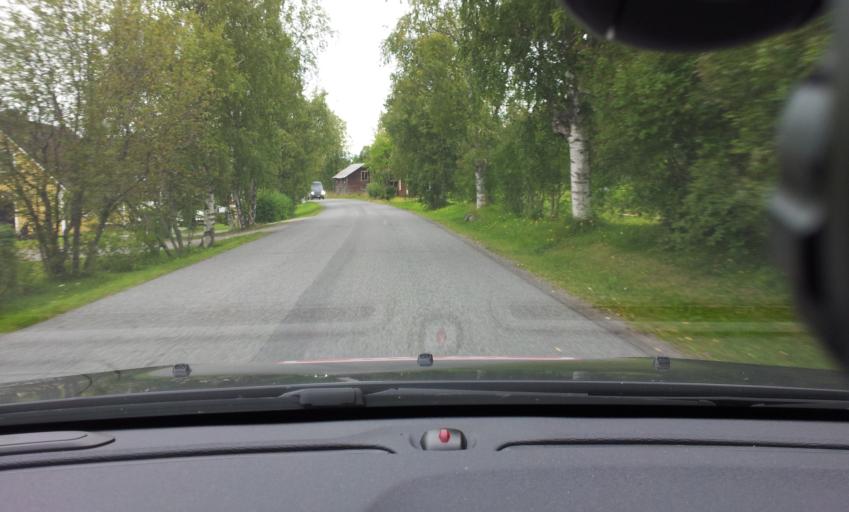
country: SE
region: Jaemtland
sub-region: OEstersunds Kommun
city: Brunflo
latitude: 63.0384
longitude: 14.8776
